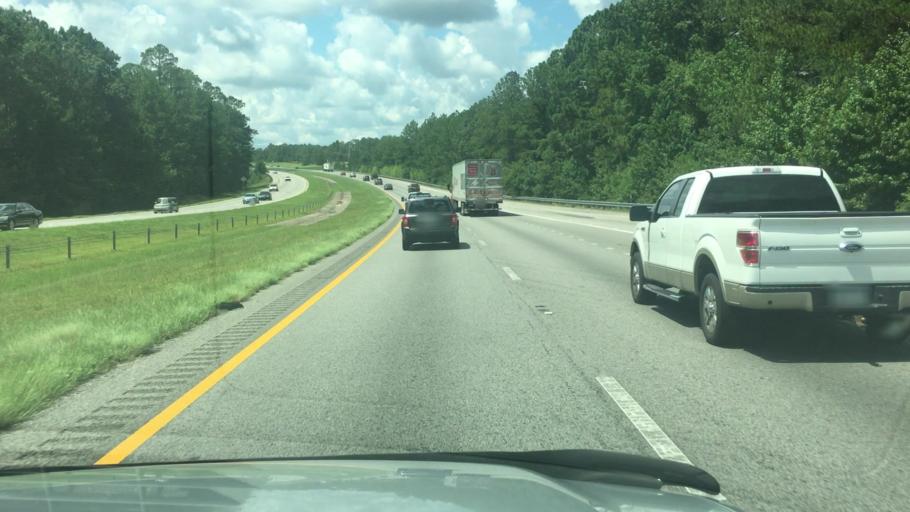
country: US
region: South Carolina
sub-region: Kershaw County
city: Lugoff
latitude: 34.1870
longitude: -80.6928
